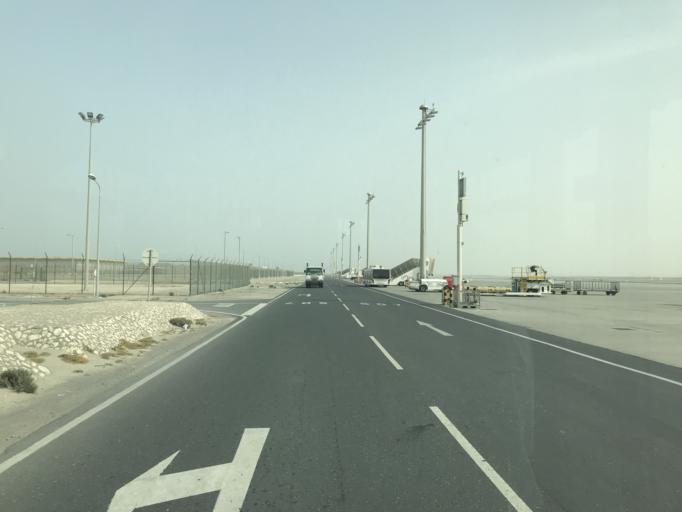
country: QA
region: Baladiyat ad Dawhah
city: Doha
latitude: 25.2767
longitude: 51.5999
